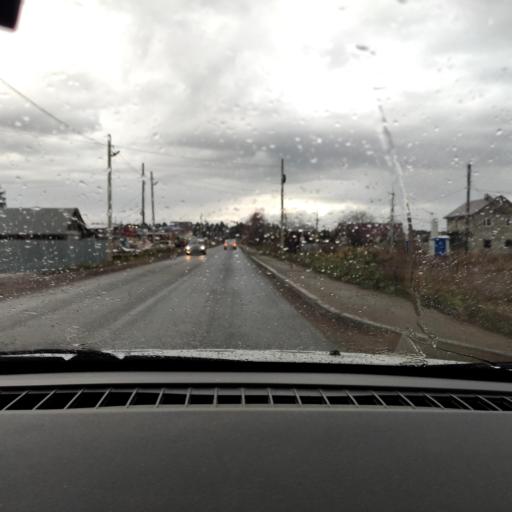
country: RU
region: Perm
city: Kultayevo
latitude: 57.8975
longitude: 55.9634
